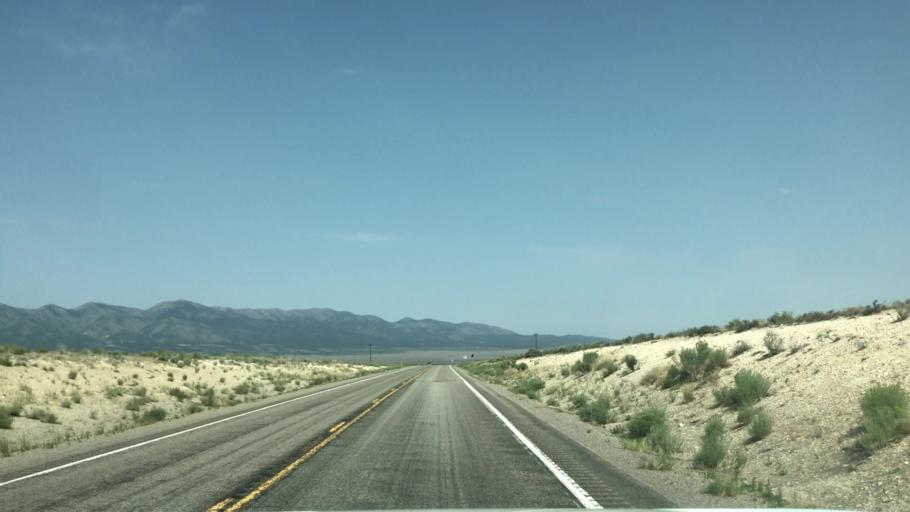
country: US
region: Nevada
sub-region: White Pine County
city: Ely
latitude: 39.0383
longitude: -114.7118
